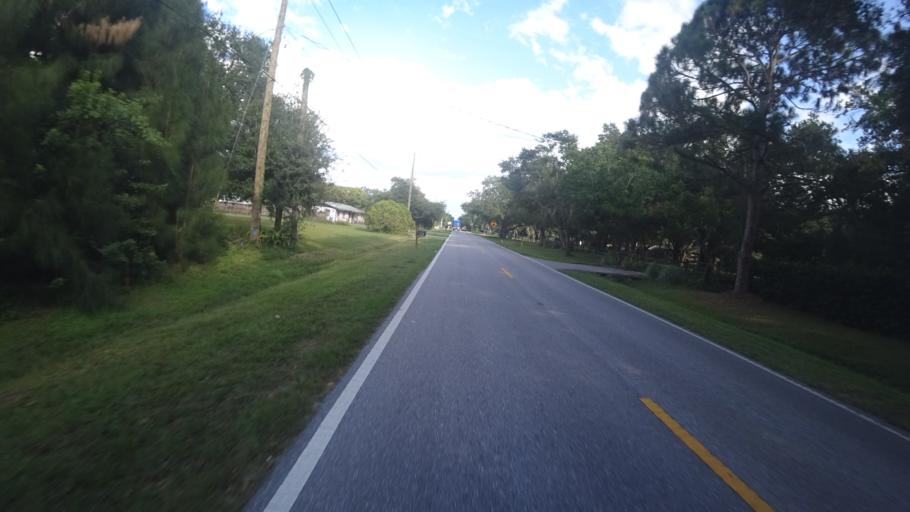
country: US
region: Florida
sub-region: Manatee County
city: Samoset
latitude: 27.4767
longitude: -82.5073
